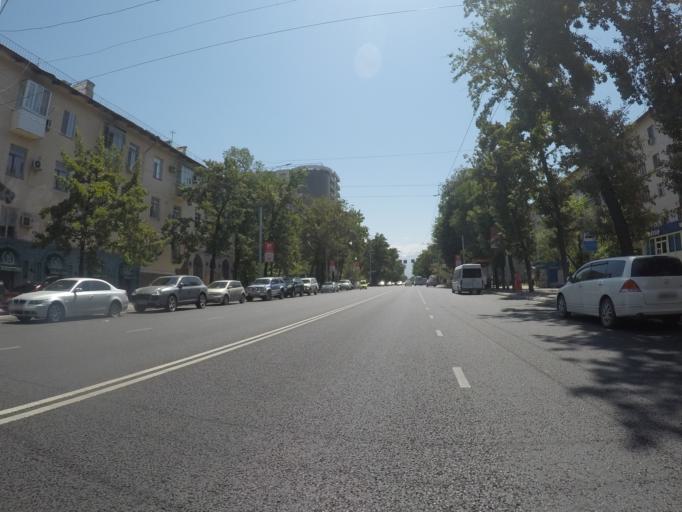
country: KG
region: Chuy
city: Bishkek
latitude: 42.8739
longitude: 74.5880
